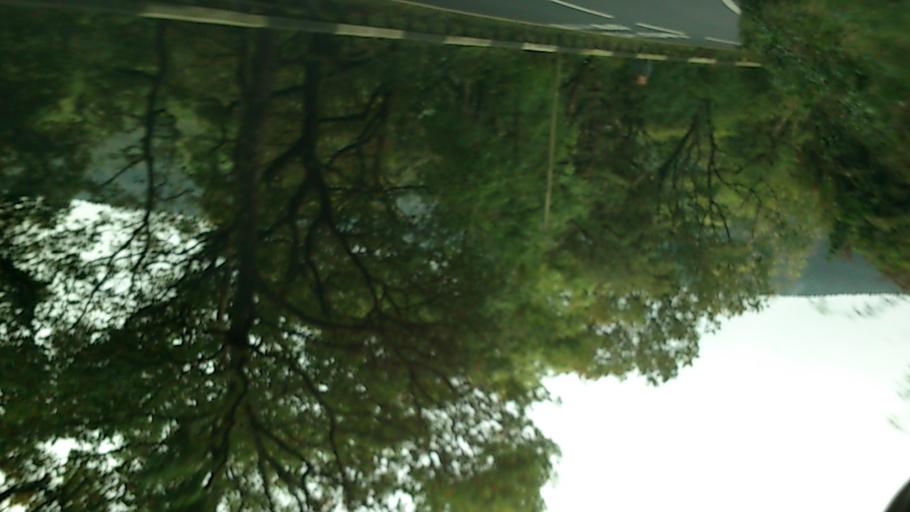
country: GB
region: Wales
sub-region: Gwynedd
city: Bala
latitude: 52.7010
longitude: -3.6245
